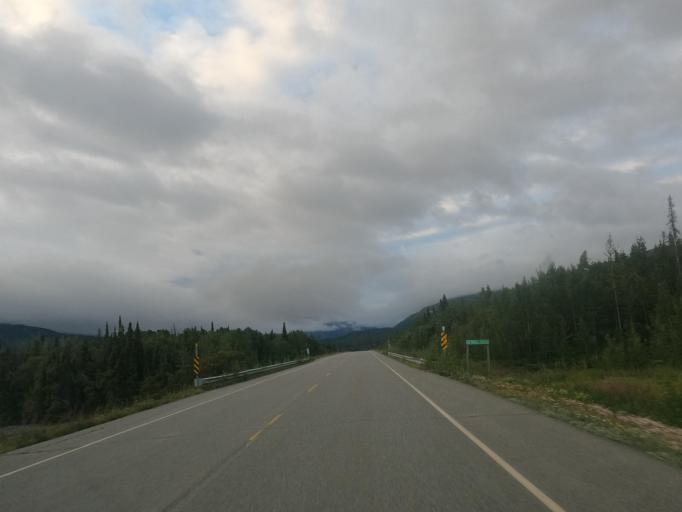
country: CA
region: Yukon
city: Haines Junction
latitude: 60.3059
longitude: -137.0383
